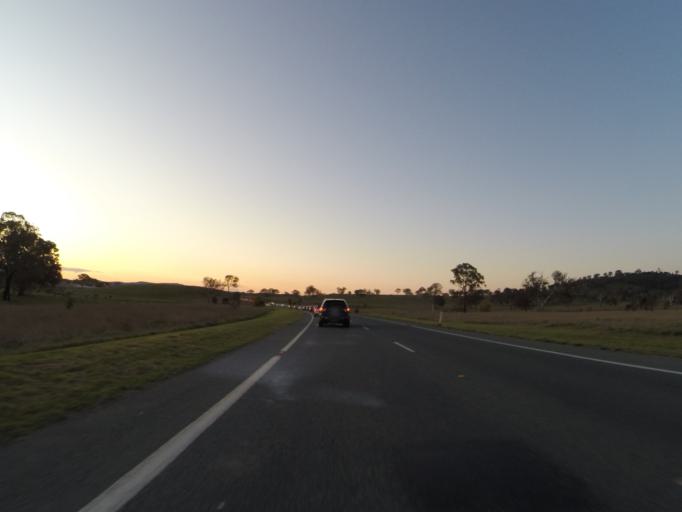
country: AU
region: Australian Capital Territory
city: Kaleen
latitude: -35.2046
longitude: 149.1695
